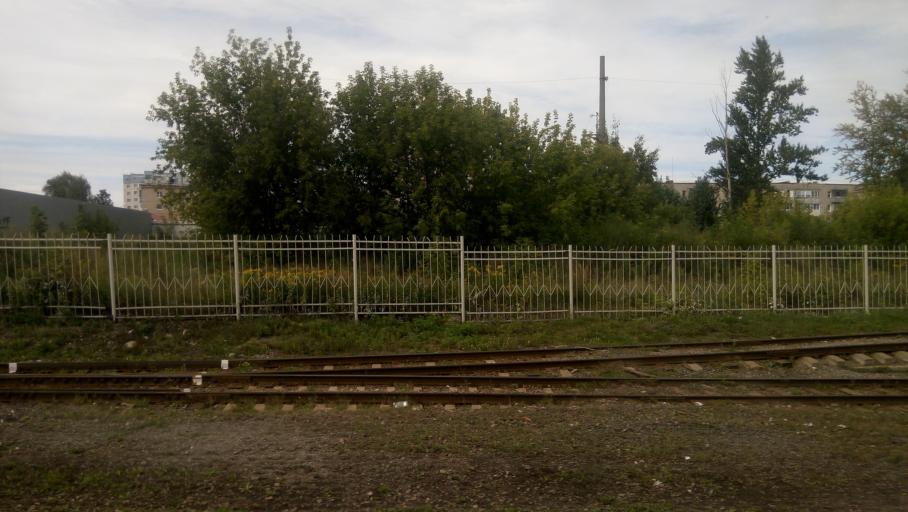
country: RU
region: Moskovskaya
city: Pavlovskiy Posad
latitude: 55.7760
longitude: 38.6659
